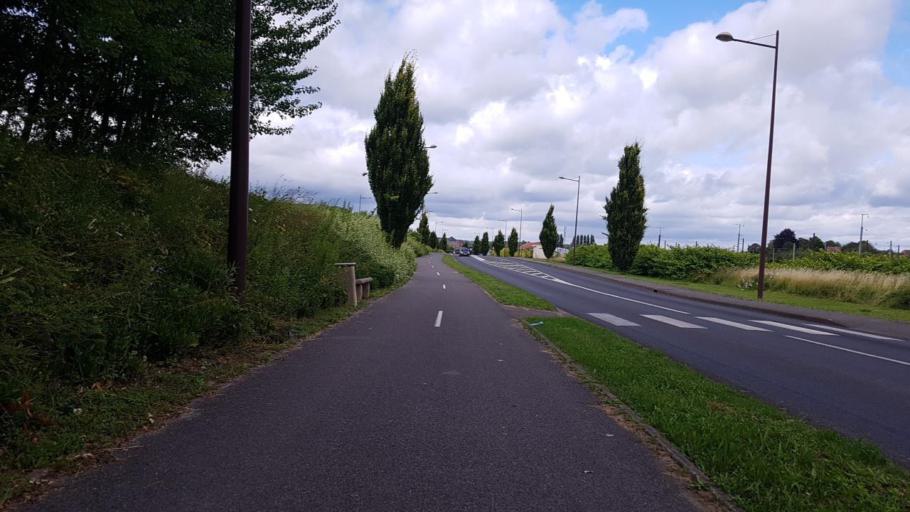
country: FR
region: Picardie
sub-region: Departement de l'Aisne
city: Hirson
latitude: 49.9109
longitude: 4.0777
